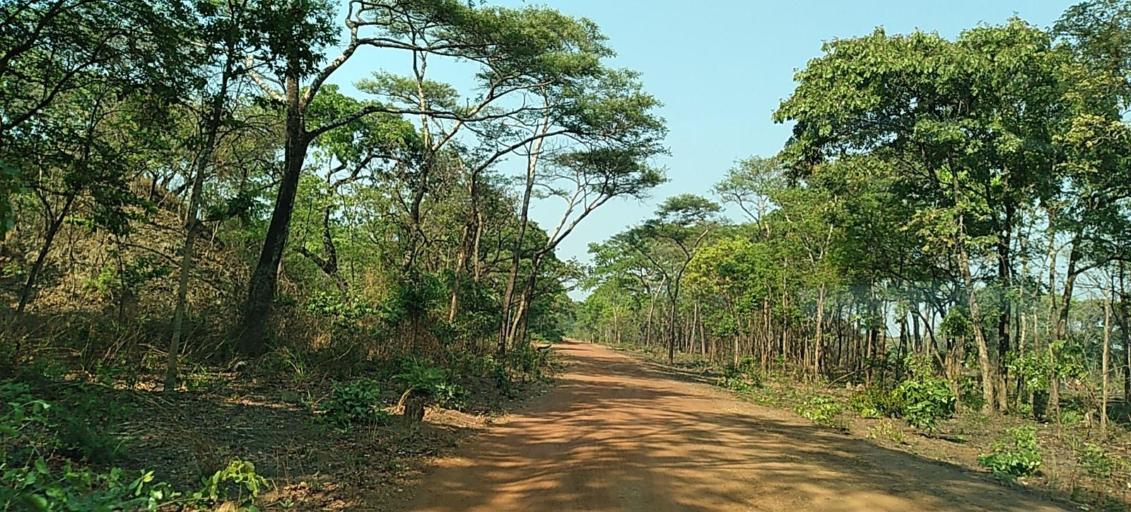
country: ZM
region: Copperbelt
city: Chingola
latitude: -12.8712
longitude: 27.4525
